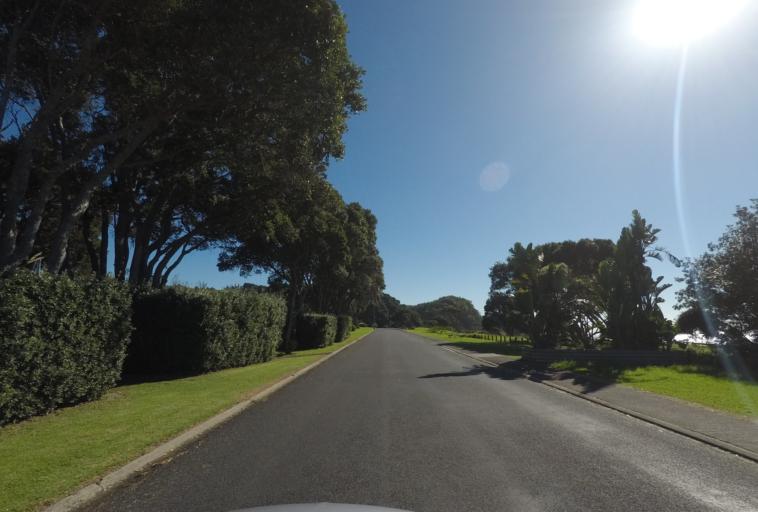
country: NZ
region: Waikato
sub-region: Thames-Coromandel District
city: Whangamata
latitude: -37.2815
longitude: 175.9016
